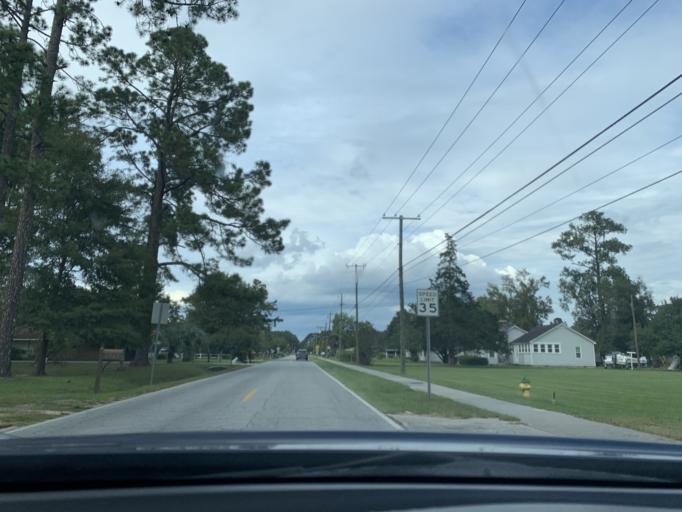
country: US
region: Georgia
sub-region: Chatham County
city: Pooler
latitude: 32.1020
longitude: -81.2537
